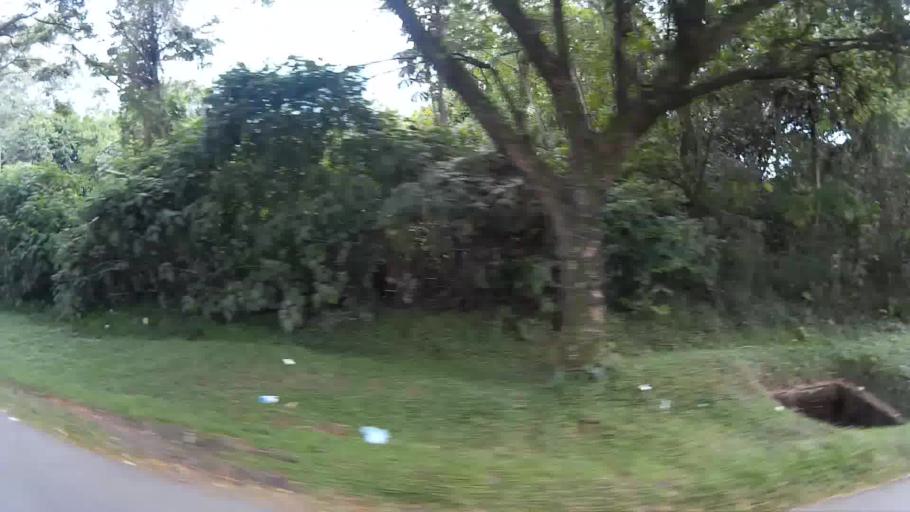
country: CO
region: Risaralda
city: Pereira
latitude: 4.8137
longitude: -75.7856
